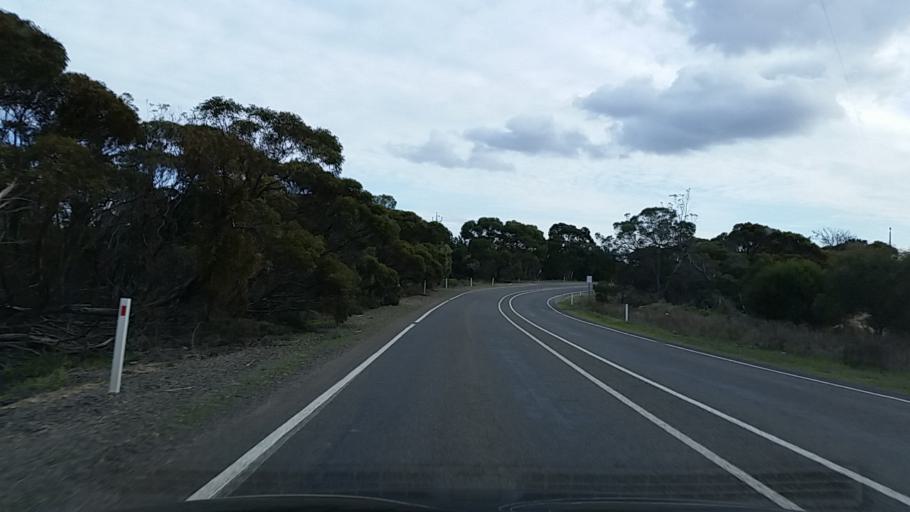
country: AU
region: South Australia
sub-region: Mount Barker
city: Callington
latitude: -35.1182
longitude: 139.1490
